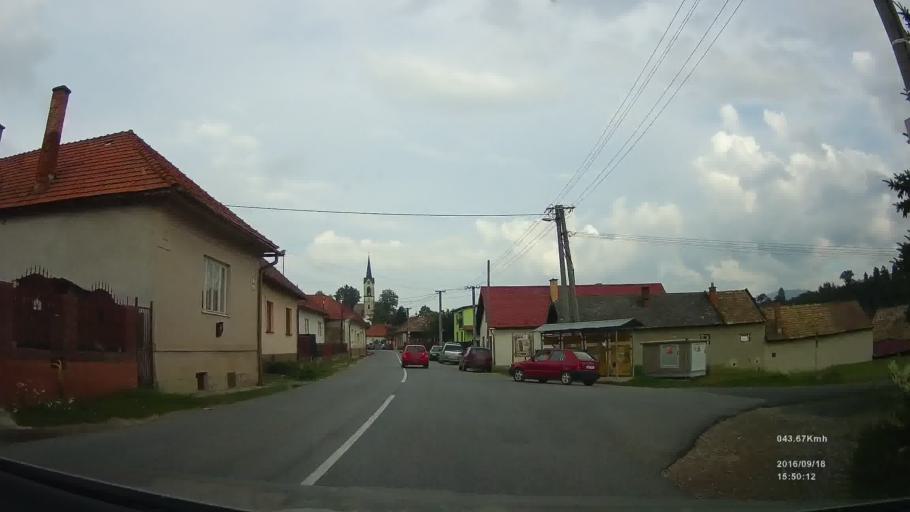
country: SK
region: Kosicky
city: Spisska Nova Ves
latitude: 48.9148
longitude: 20.6164
